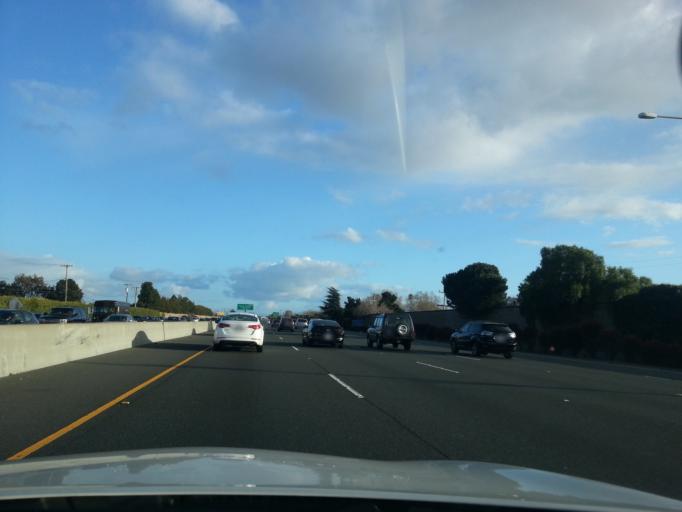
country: US
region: California
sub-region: San Mateo County
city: Belmont
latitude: 37.5399
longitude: -122.2837
